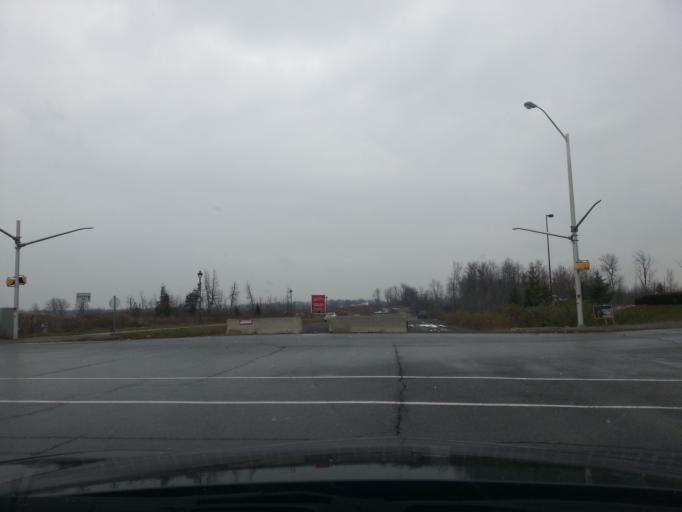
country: CA
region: Ontario
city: Carleton Place
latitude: 45.1308
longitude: -76.1185
